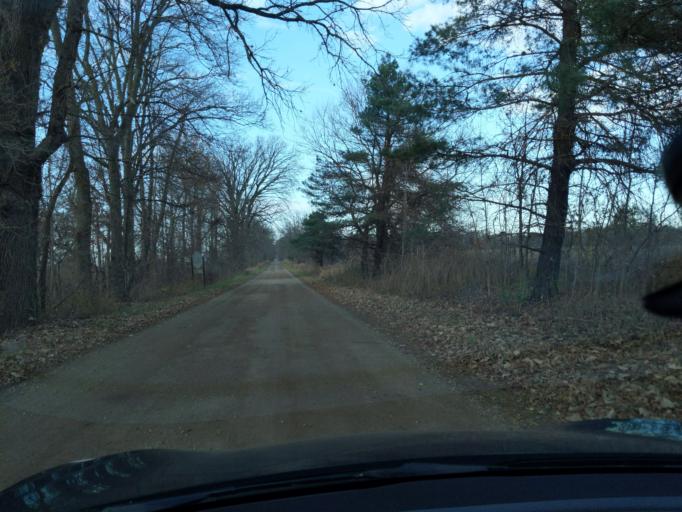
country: US
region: Michigan
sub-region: Ingham County
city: Williamston
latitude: 42.7167
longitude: -84.3249
